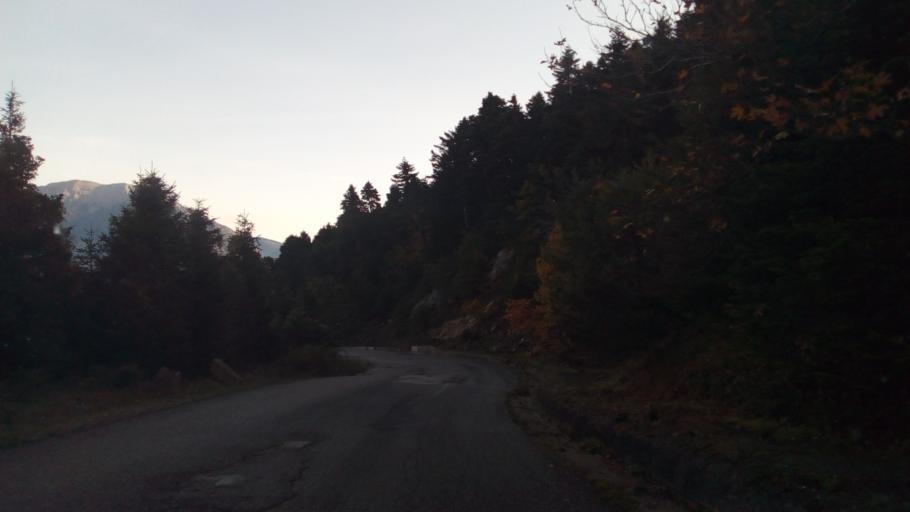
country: GR
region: West Greece
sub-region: Nomos Aitolias kai Akarnanias
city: Thermo
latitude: 38.6406
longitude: 21.8393
